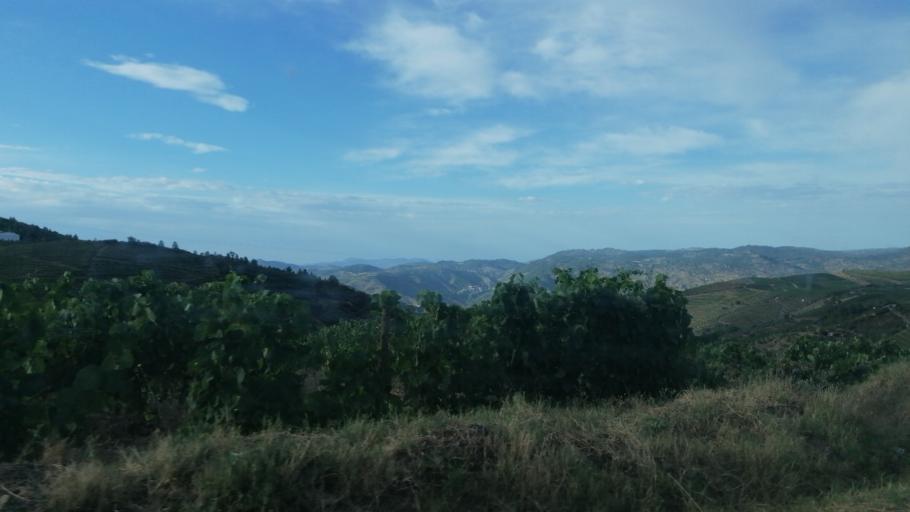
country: PT
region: Viseu
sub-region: Sao Joao da Pesqueira
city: Sao Joao da Pesqueira
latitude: 41.1526
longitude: -7.4307
